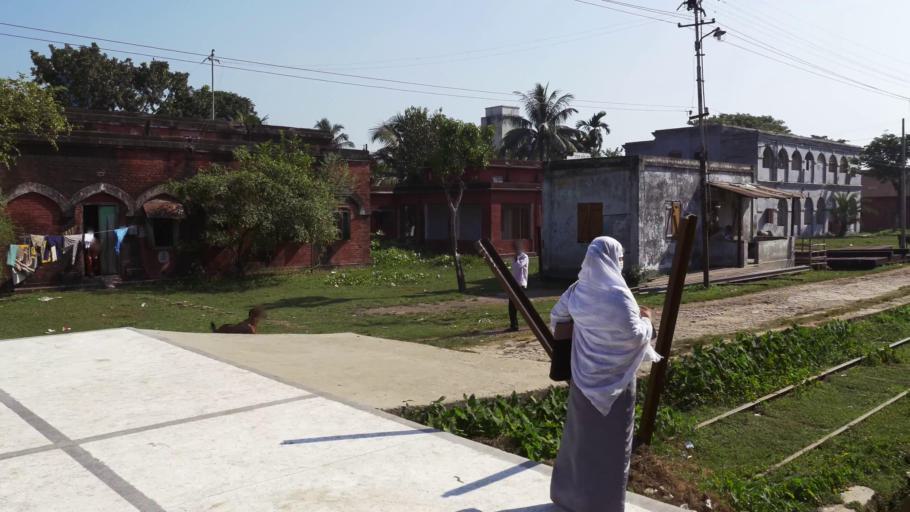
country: BD
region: Dhaka
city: Mymensingh
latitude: 24.6303
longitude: 90.4642
